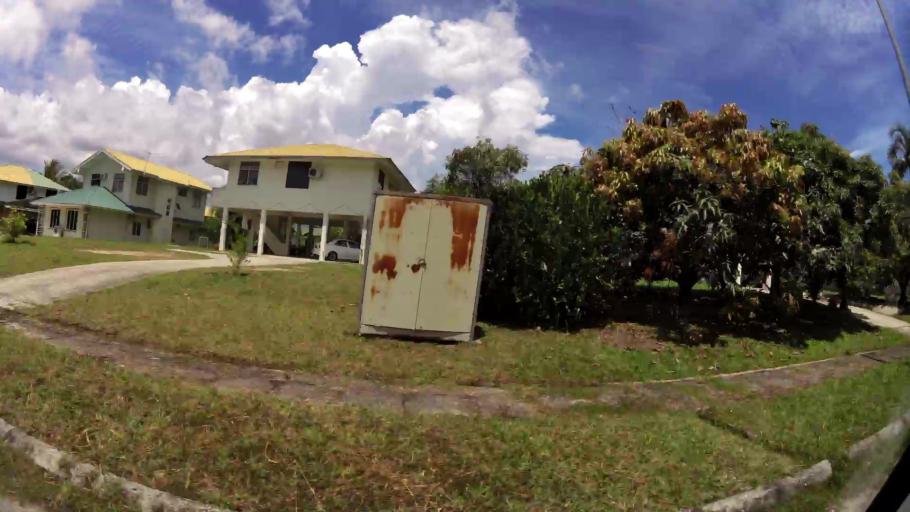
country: BN
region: Brunei and Muara
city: Bandar Seri Begawan
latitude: 4.9603
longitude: 114.9061
